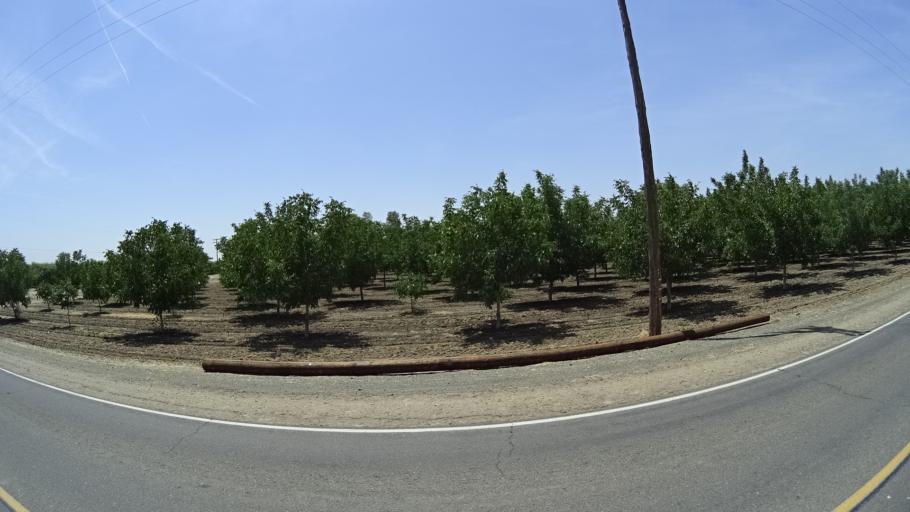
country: US
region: California
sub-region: Fresno County
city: Riverdale
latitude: 36.4021
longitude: -119.7989
